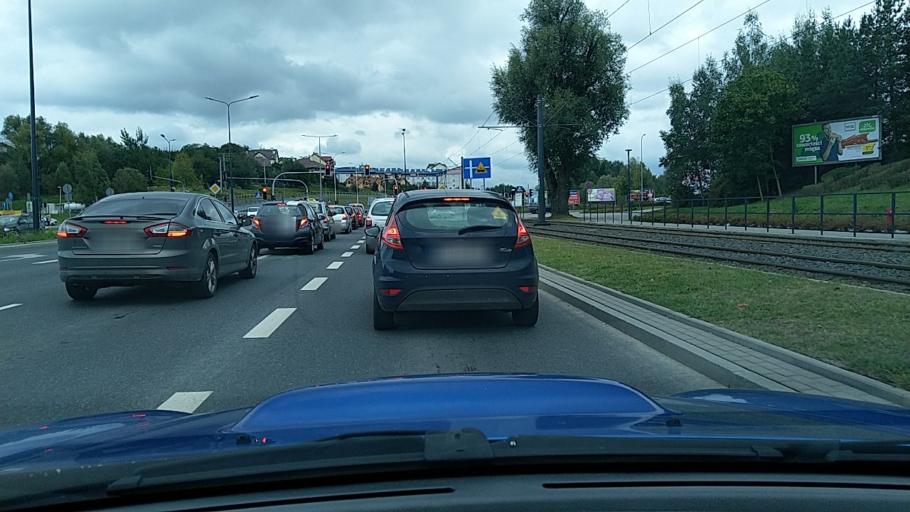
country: PL
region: Warmian-Masurian Voivodeship
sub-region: Olsztyn
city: Kortowo
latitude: 53.7411
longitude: 20.4862
